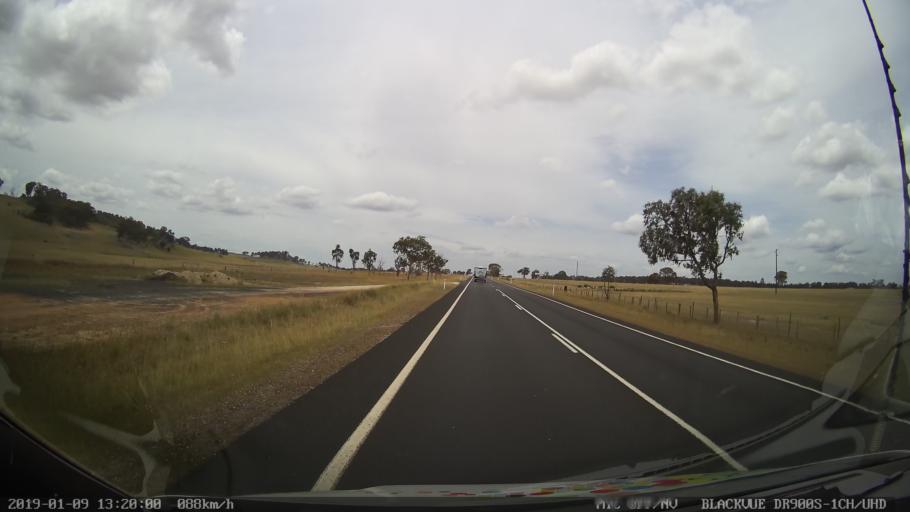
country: AU
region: New South Wales
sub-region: Armidale Dumaresq
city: Armidale
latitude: -30.5385
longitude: 151.8436
